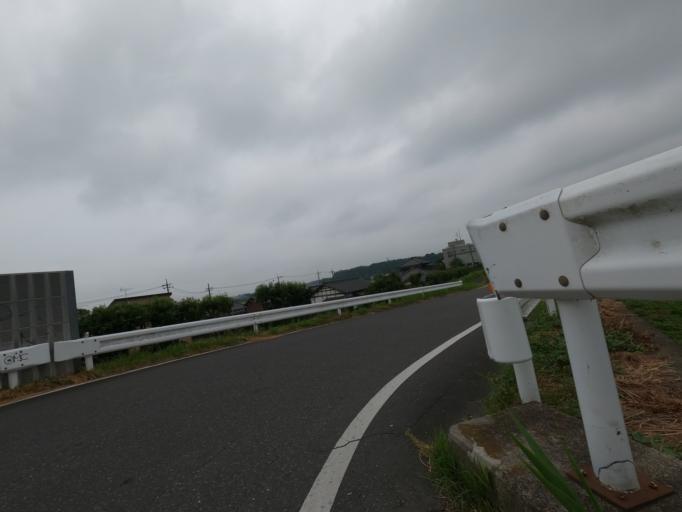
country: JP
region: Ibaraki
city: Toride
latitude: 35.9323
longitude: 140.0520
